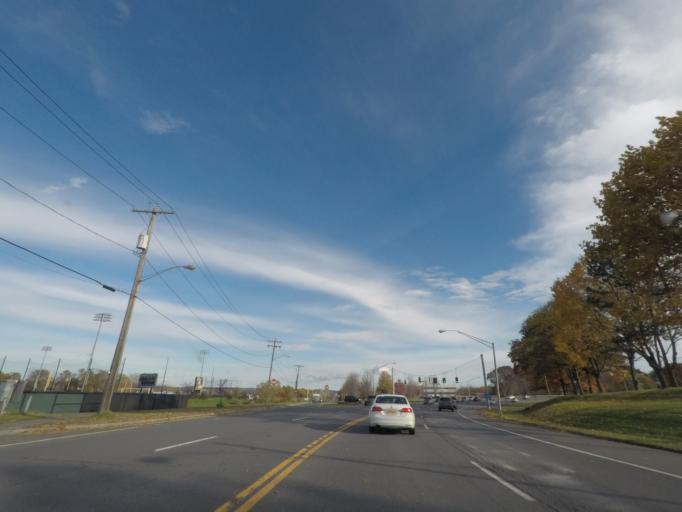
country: US
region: New York
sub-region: Albany County
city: Albany
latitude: 42.6358
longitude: -73.7769
